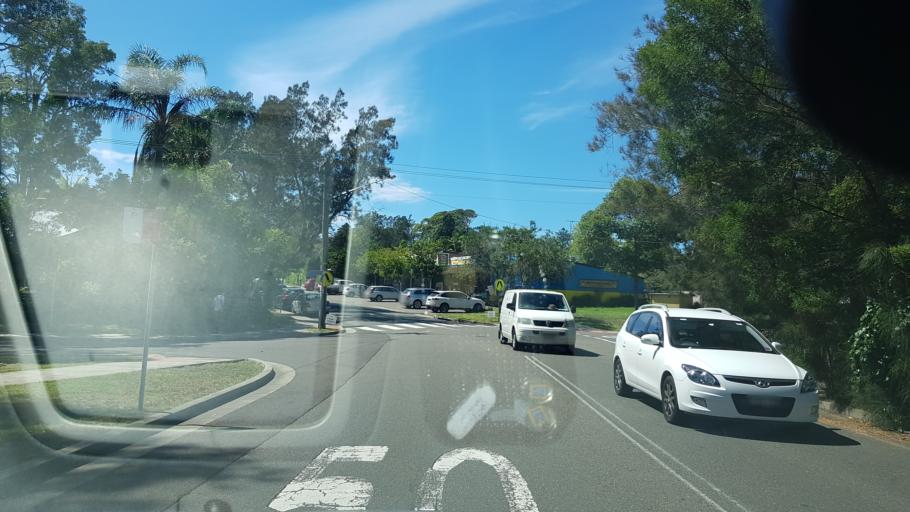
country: AU
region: New South Wales
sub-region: Pittwater
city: Bilgola Beach
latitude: -33.6274
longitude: 151.3333
